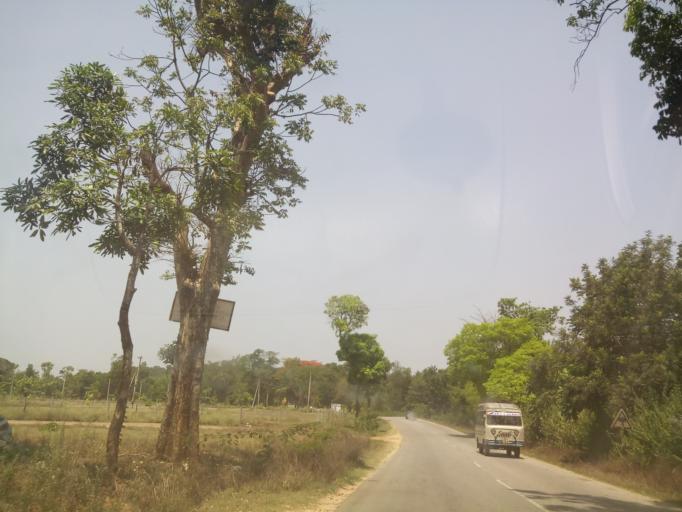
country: IN
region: Karnataka
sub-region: Hassan
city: Sakleshpur
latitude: 12.9459
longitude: 75.8733
